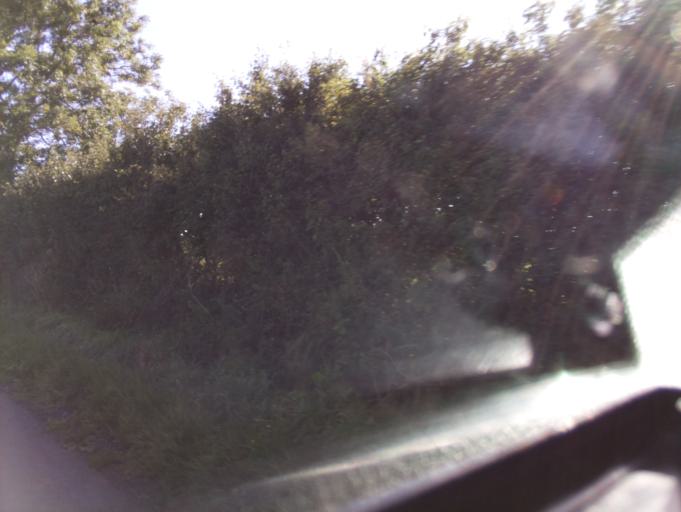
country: GB
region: England
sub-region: Bath and North East Somerset
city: Publow
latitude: 51.3954
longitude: -2.5329
